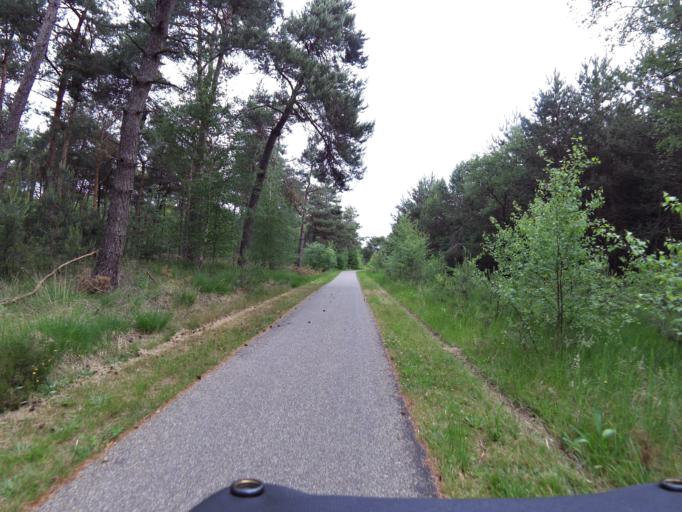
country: NL
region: North Brabant
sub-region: Gemeente Hilvarenbeek
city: Hilvarenbeek
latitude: 51.4072
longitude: 5.1103
